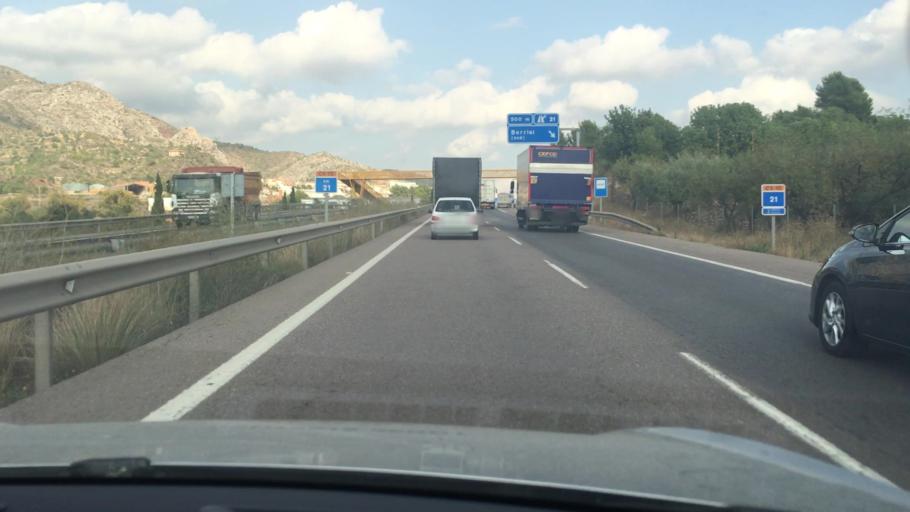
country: ES
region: Valencia
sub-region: Provincia de Castello
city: Borriol
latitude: 40.0310
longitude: -0.0843
